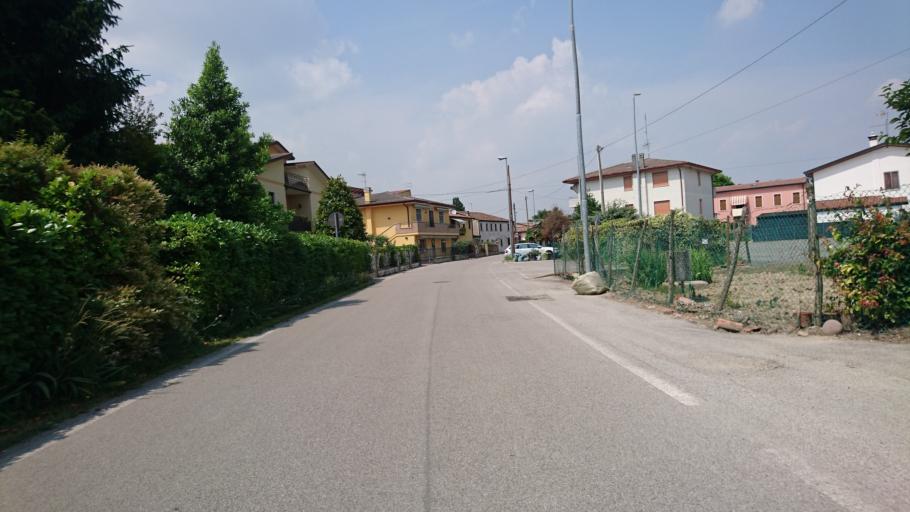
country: IT
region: Veneto
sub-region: Provincia di Padova
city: Masera di Padova
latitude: 45.3025
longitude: 11.8541
